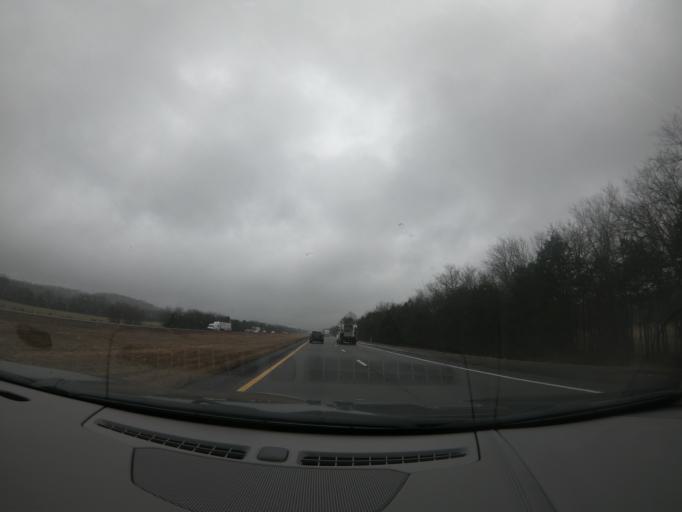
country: US
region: Tennessee
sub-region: Rutherford County
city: Plainview
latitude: 35.6842
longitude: -86.2913
